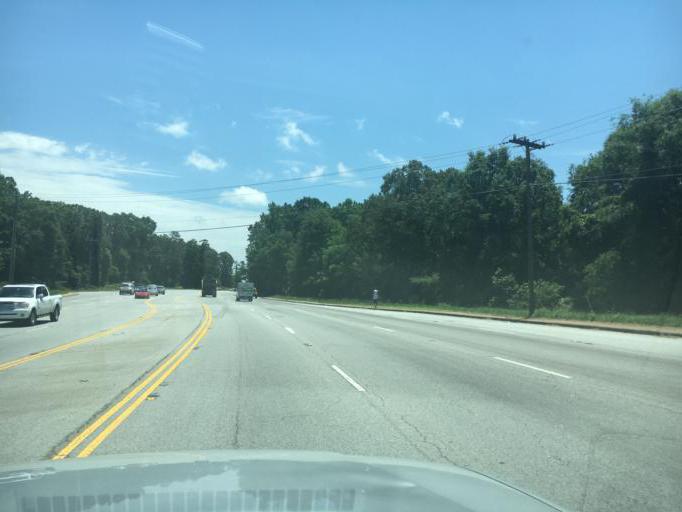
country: US
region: South Carolina
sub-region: Greenville County
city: Berea
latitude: 34.9145
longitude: -82.4619
